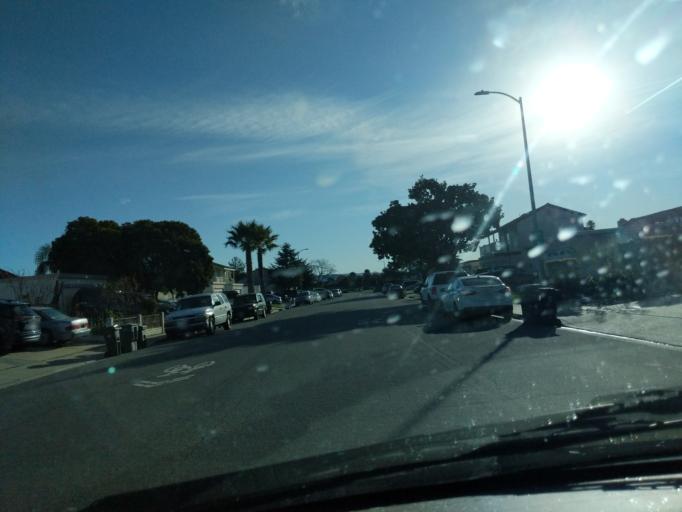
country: US
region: California
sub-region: Monterey County
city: Boronda
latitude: 36.7112
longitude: -121.6602
